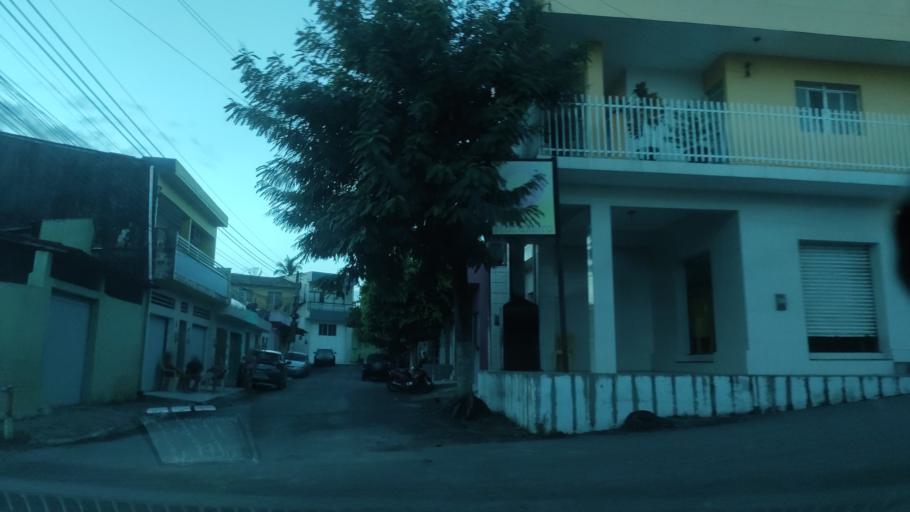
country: BR
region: Alagoas
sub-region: Uniao Dos Palmares
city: Uniao dos Palmares
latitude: -9.1552
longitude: -36.0288
